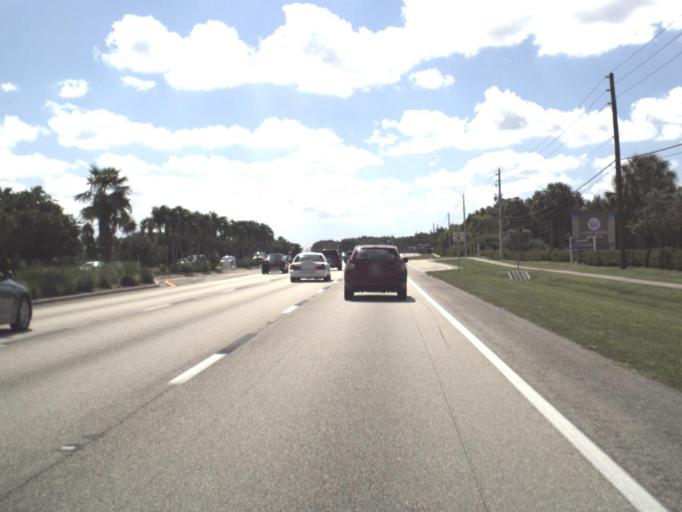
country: US
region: Florida
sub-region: Lee County
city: Estero
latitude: 26.4190
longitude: -81.8119
